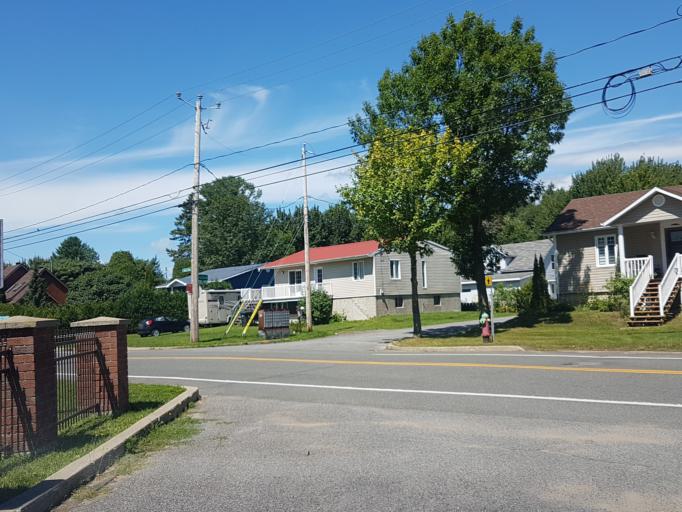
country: CA
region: Quebec
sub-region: Mauricie
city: Nicolet
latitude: 46.2789
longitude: -72.6682
